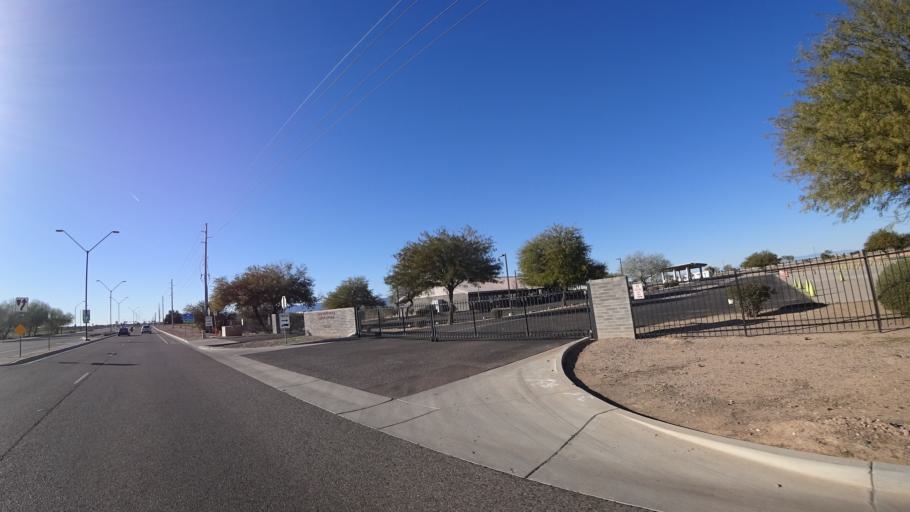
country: US
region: Arizona
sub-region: Maricopa County
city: Goodyear
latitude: 33.4499
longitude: -112.3689
